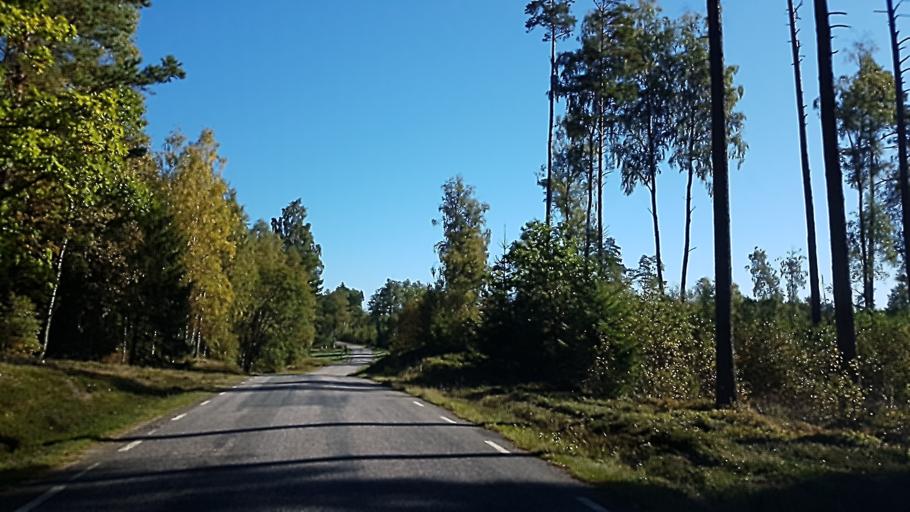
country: SE
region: Kronoberg
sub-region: Ljungby Kommun
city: Ljungby
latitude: 56.8185
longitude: 14.0425
